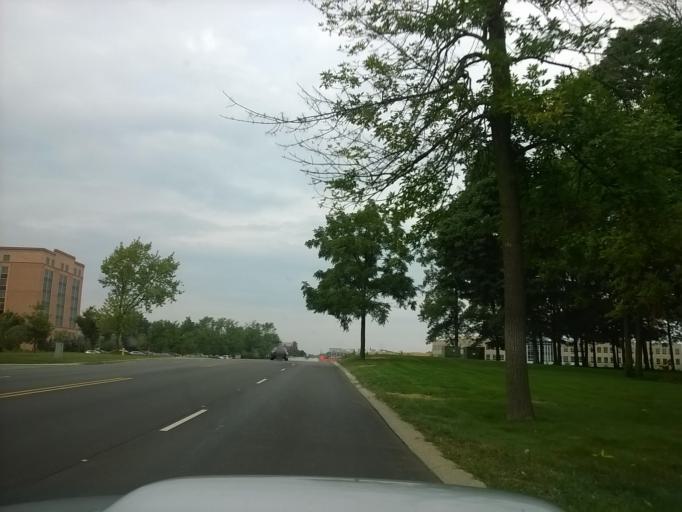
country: US
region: Indiana
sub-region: Hamilton County
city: Carmel
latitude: 39.9628
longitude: -86.1551
